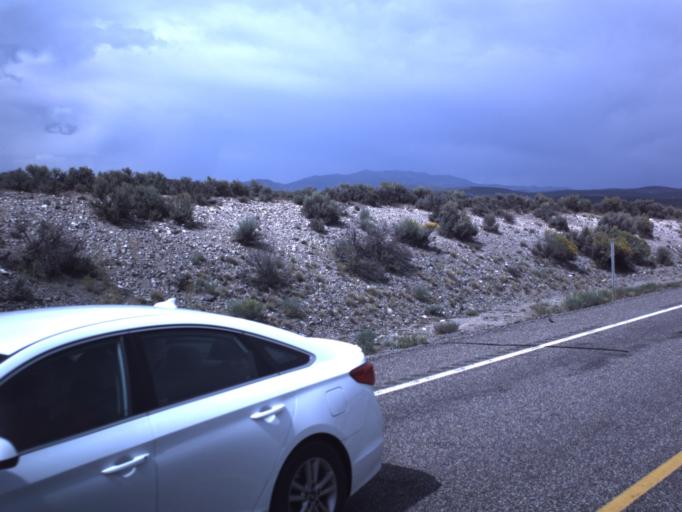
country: US
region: Utah
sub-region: Garfield County
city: Panguitch
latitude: 37.9834
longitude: -112.3987
